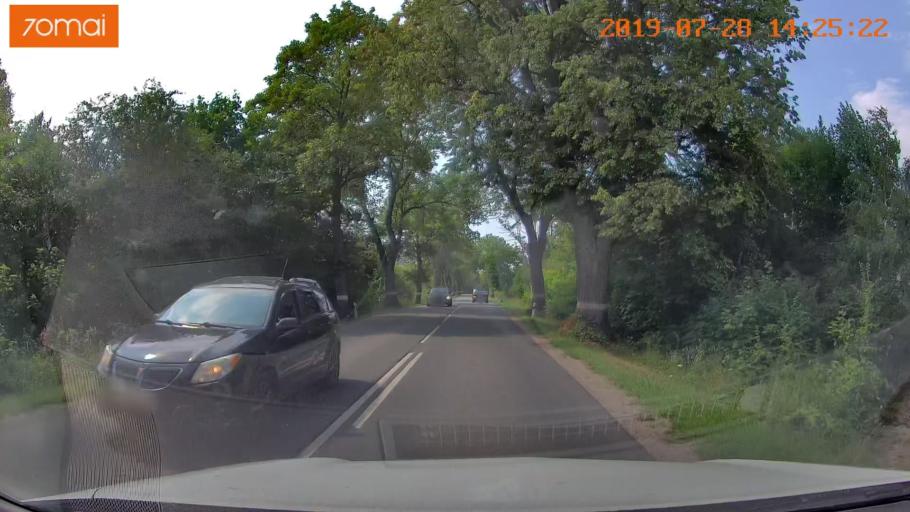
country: RU
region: Kaliningrad
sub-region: Gorod Svetlogorsk
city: Svetlogorsk
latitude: 54.8129
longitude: 20.1342
